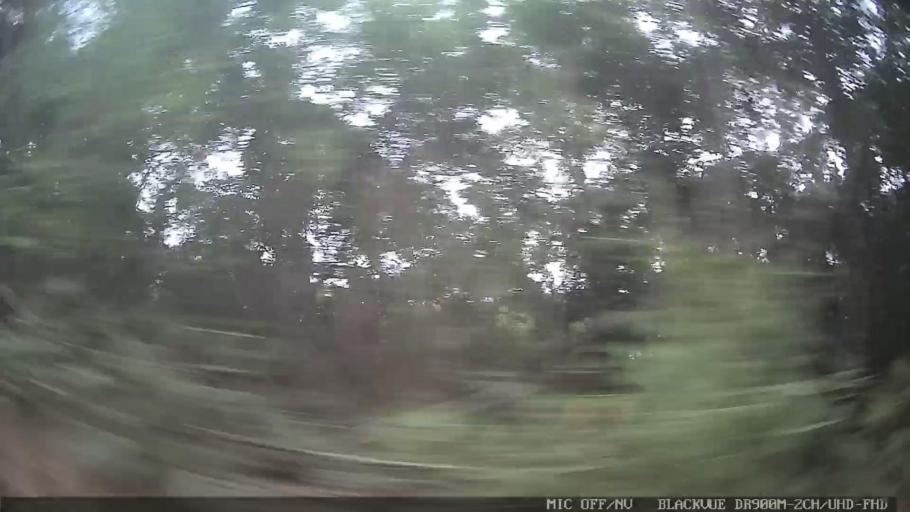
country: BR
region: Sao Paulo
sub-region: Suzano
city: Suzano
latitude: -23.6765
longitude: -46.2359
